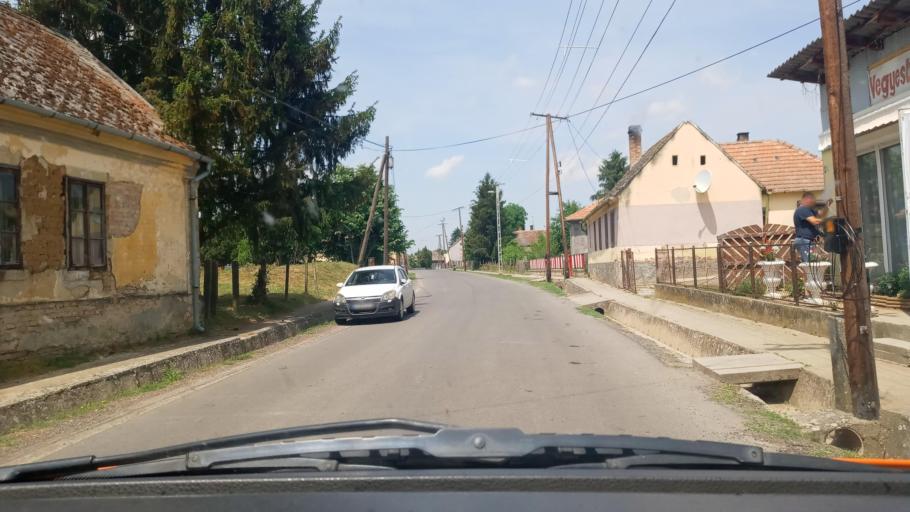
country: HU
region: Baranya
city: Szigetvar
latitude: 45.9845
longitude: 17.7038
